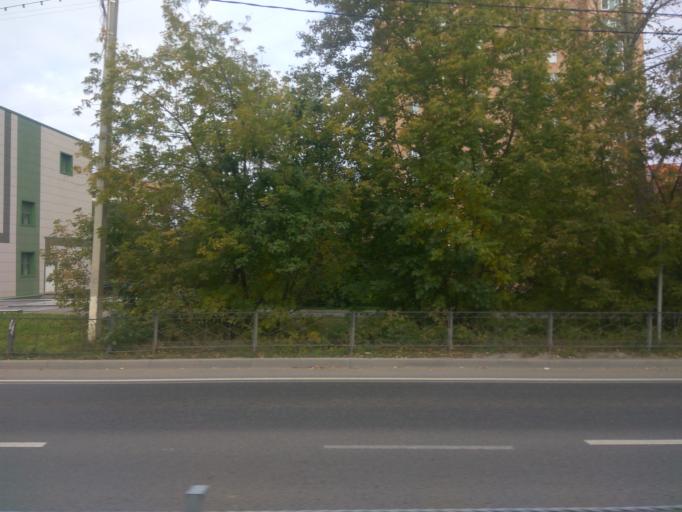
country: RU
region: Moskovskaya
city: Fryazino
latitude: 55.9557
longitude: 38.0605
